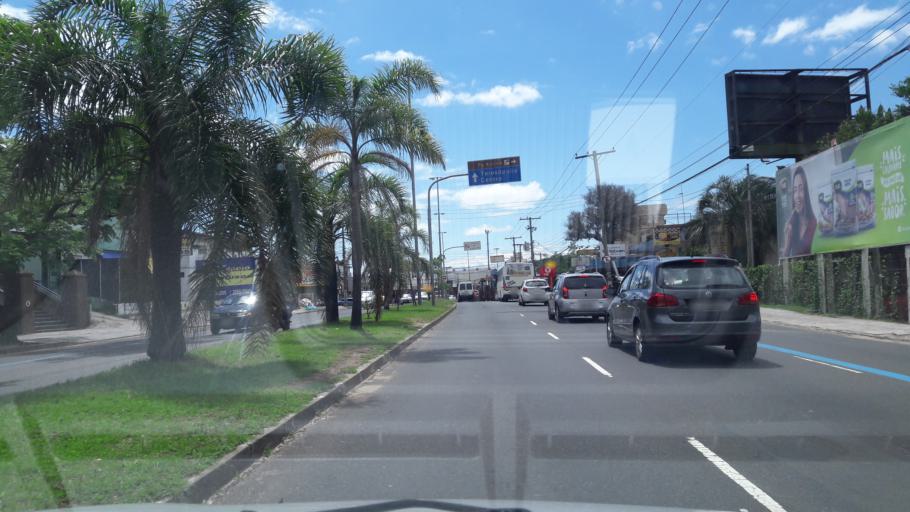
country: BR
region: Rio Grande do Sul
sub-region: Porto Alegre
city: Porto Alegre
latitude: -30.1035
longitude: -51.2303
